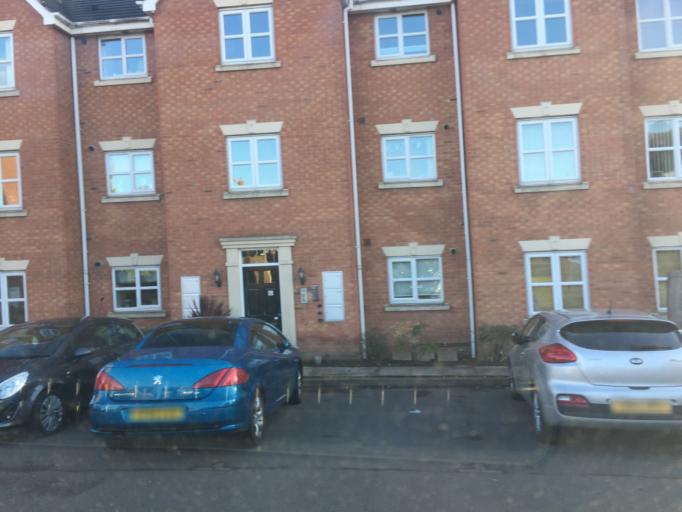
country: GB
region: England
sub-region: Walsall
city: Darlaston
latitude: 52.5612
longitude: -2.0266
